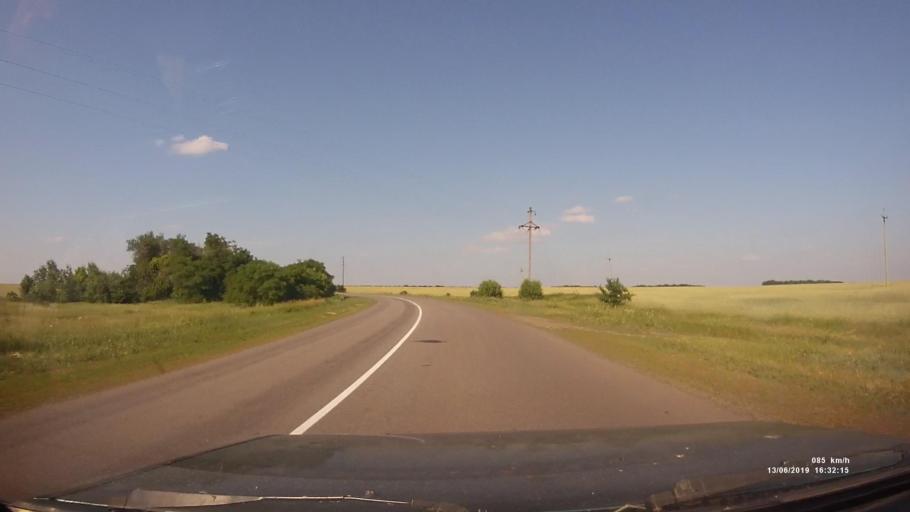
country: RU
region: Rostov
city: Kazanskaya
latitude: 49.8464
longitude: 41.2692
